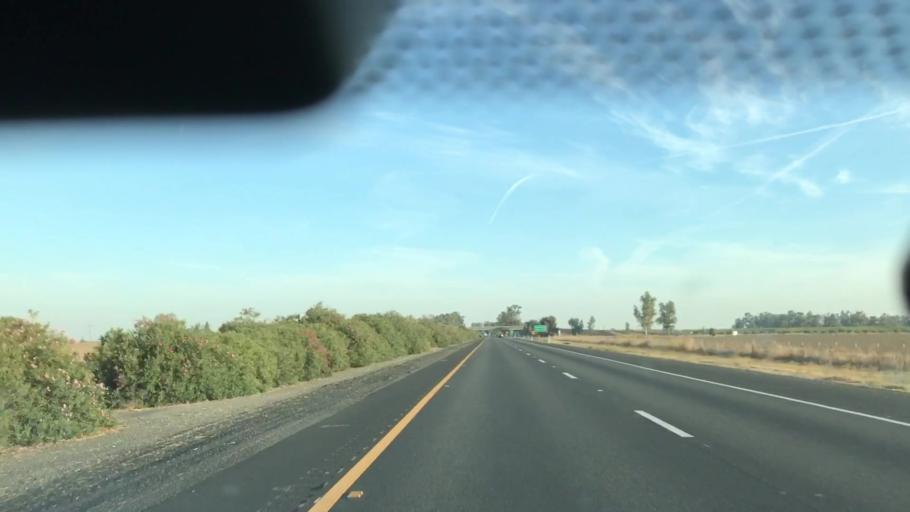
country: US
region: California
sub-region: Glenn County
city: Willows
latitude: 39.5768
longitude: -122.2112
